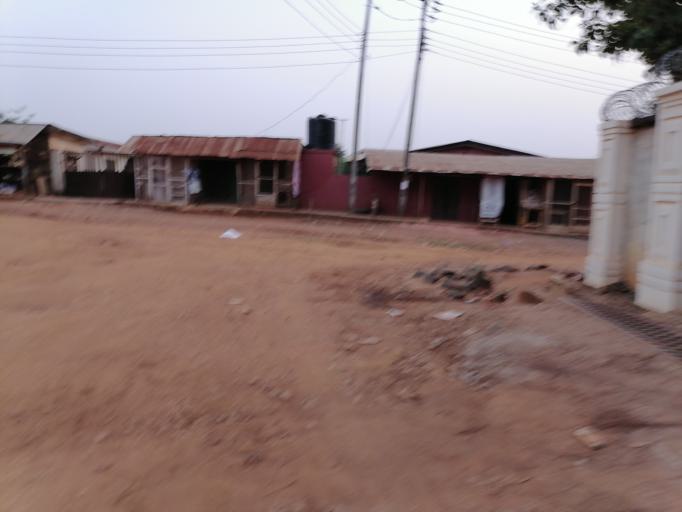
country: NG
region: Ondo
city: Akure
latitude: 7.2864
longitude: 5.1490
